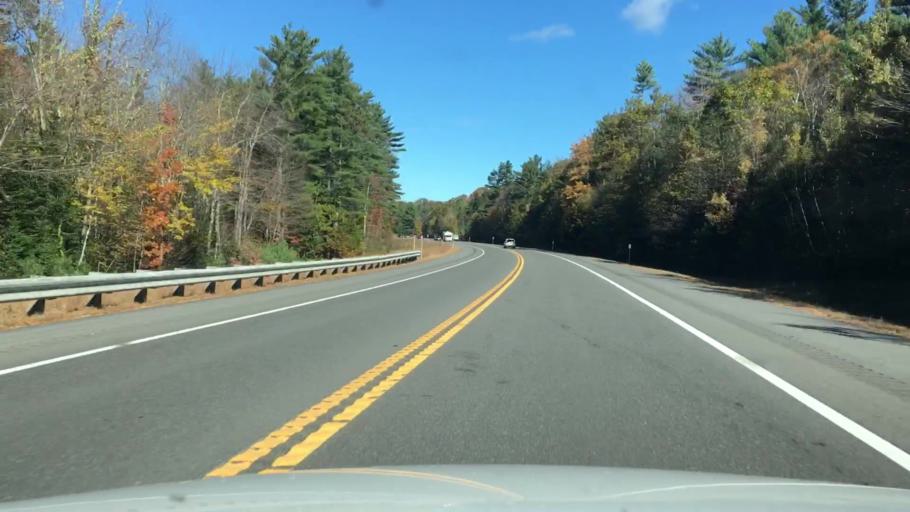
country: US
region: New Hampshire
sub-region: Strafford County
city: Farmington
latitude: 43.4540
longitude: -70.9941
